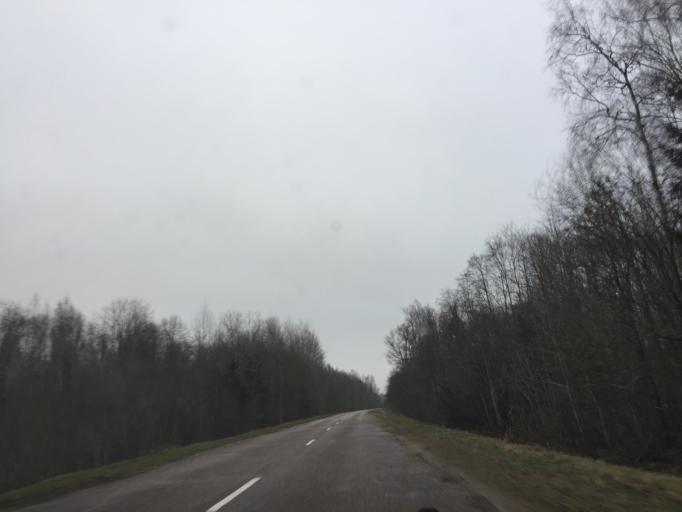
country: LV
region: Limbazu Rajons
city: Limbazi
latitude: 57.5430
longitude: 24.6800
